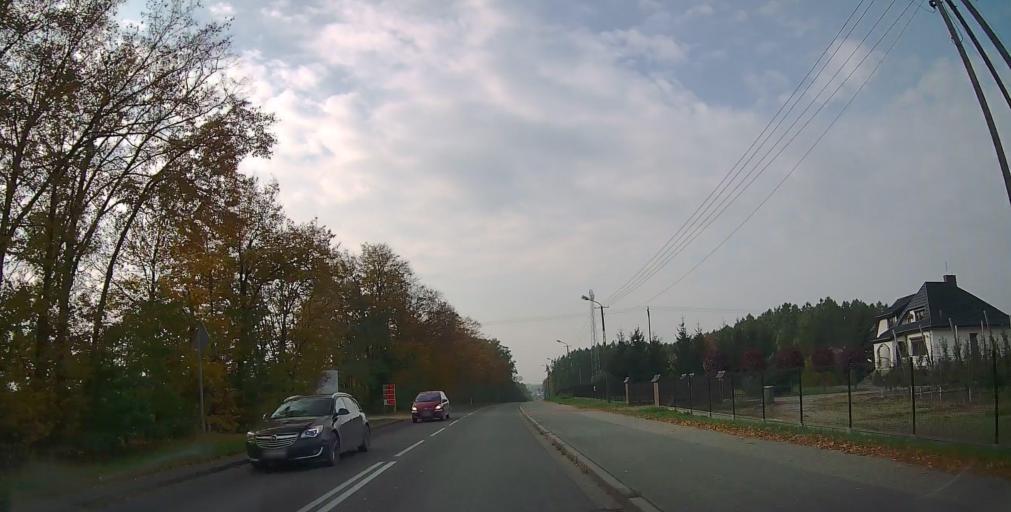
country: PL
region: Masovian Voivodeship
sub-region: Powiat grojecki
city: Mogielnica
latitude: 51.7021
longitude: 20.7338
